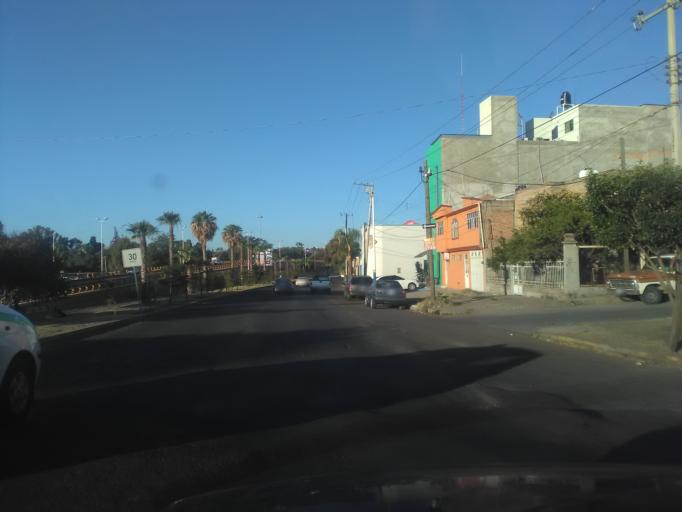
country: MX
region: Durango
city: Victoria de Durango
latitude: 24.0316
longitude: -104.6859
